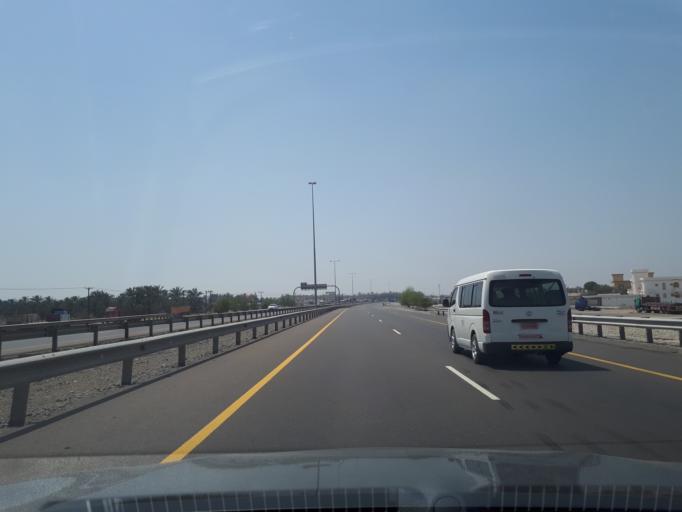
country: OM
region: Al Batinah
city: Al Liwa'
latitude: 24.5030
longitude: 56.5678
